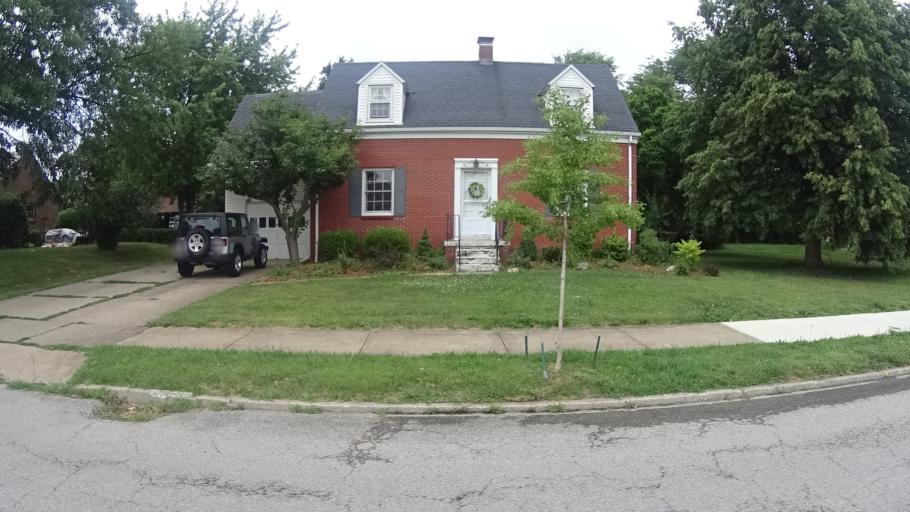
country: US
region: Ohio
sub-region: Erie County
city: Sandusky
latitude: 41.4344
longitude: -82.6943
